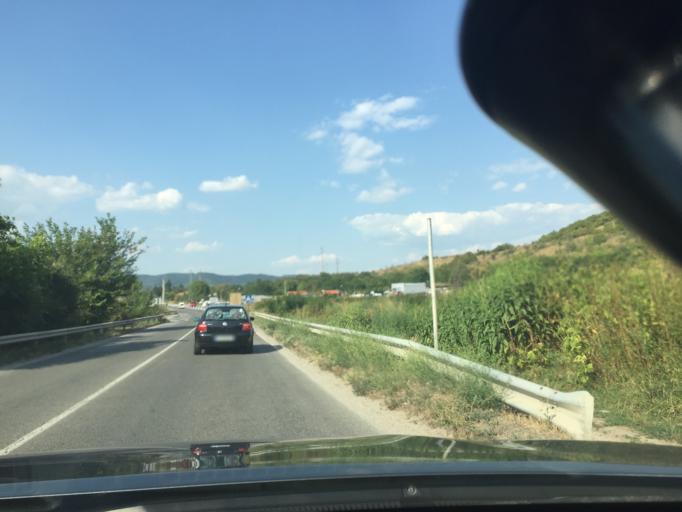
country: BG
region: Kyustendil
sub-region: Obshtina Dupnitsa
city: Dupnitsa
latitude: 42.2299
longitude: 23.0830
